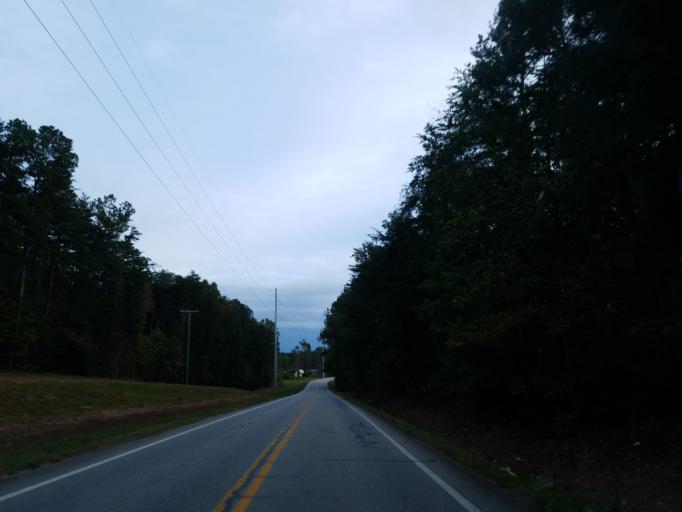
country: US
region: Georgia
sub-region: Dawson County
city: Dawsonville
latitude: 34.4613
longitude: -84.1739
